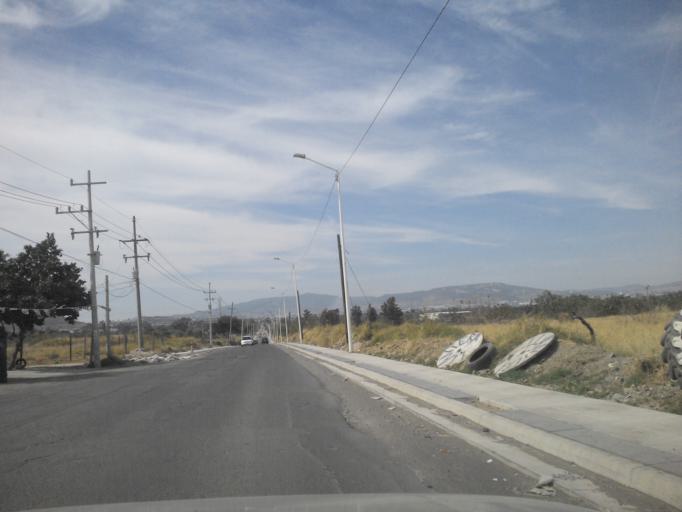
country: MX
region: Jalisco
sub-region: Tlajomulco de Zuniga
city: Colinas del Roble
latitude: 20.5103
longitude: -103.4025
